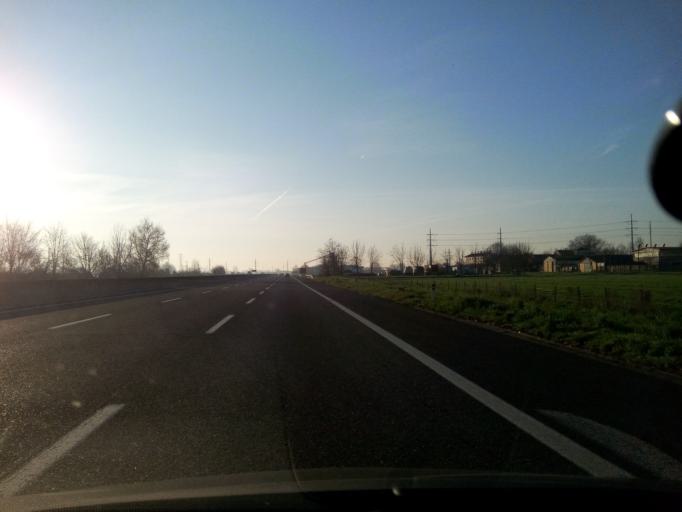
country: IT
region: Lombardy
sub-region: Provincia di Lodi
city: Somaglia
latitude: 45.1357
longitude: 9.6464
